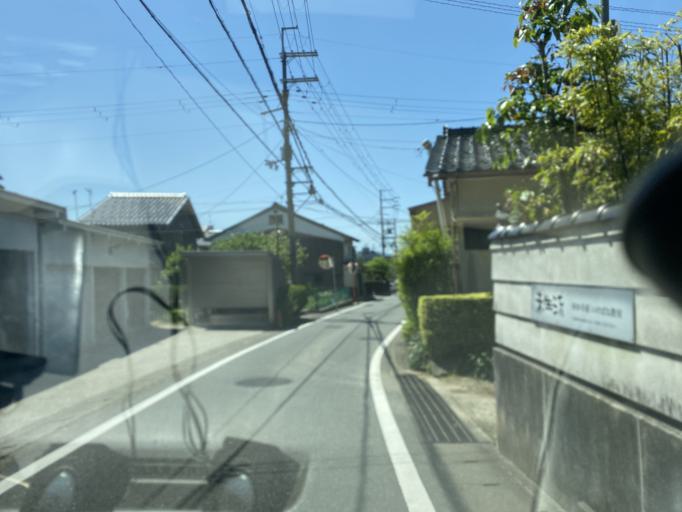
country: JP
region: Hyogo
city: Toyooka
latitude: 35.5388
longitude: 134.8196
